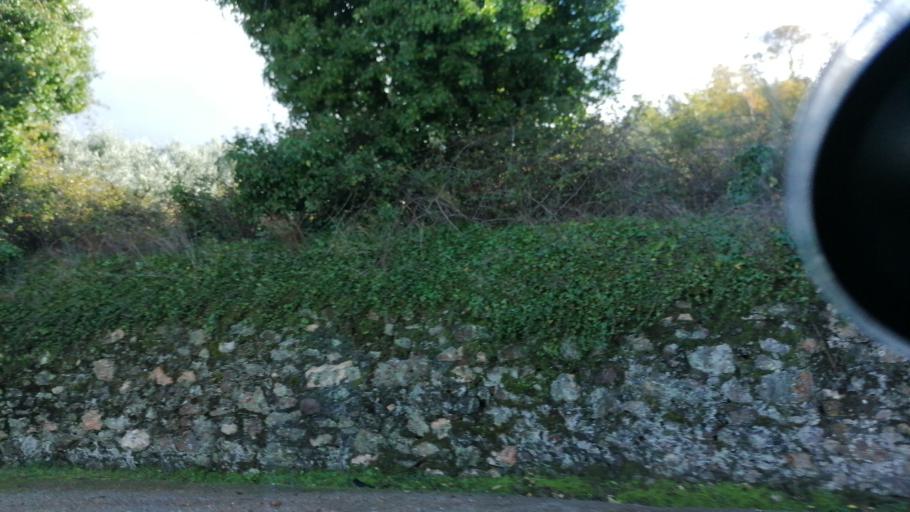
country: PT
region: Vila Real
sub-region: Peso da Regua
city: Peso da Regua
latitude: 41.1286
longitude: -7.7882
